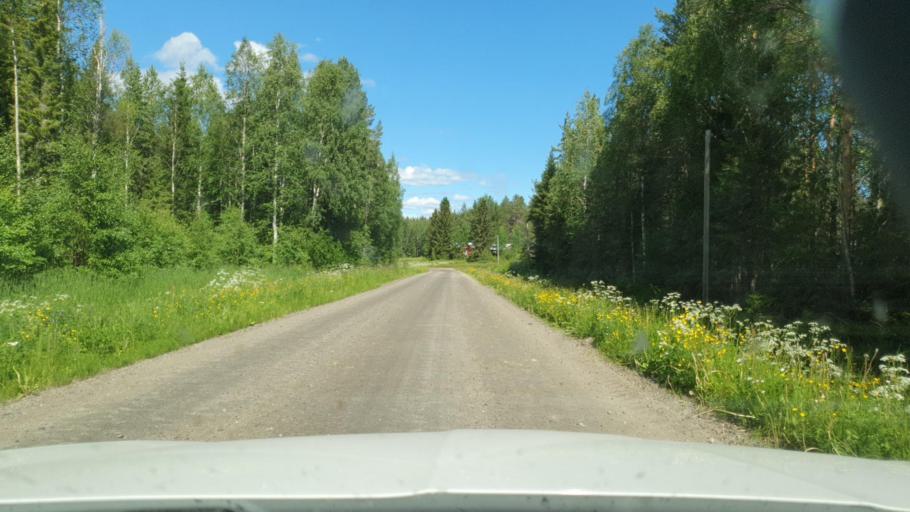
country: SE
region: Vaesterbotten
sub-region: Skelleftea Kommun
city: Backa
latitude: 65.1544
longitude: 21.1605
